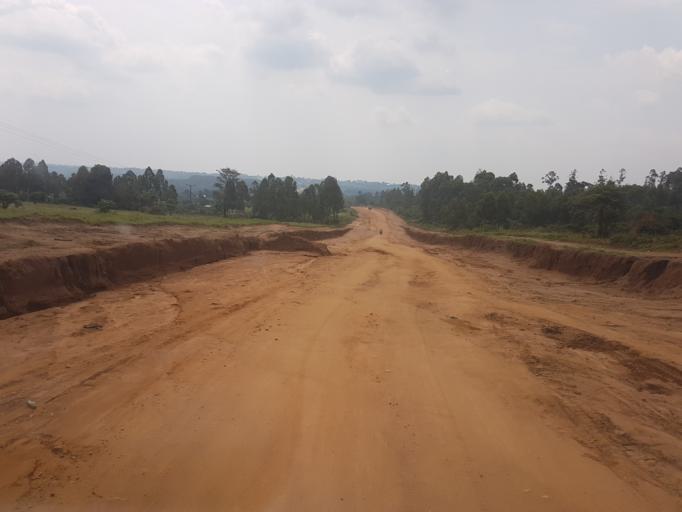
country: UG
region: Western Region
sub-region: Kanungu District
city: Ntungamo
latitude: -0.8133
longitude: 29.7064
